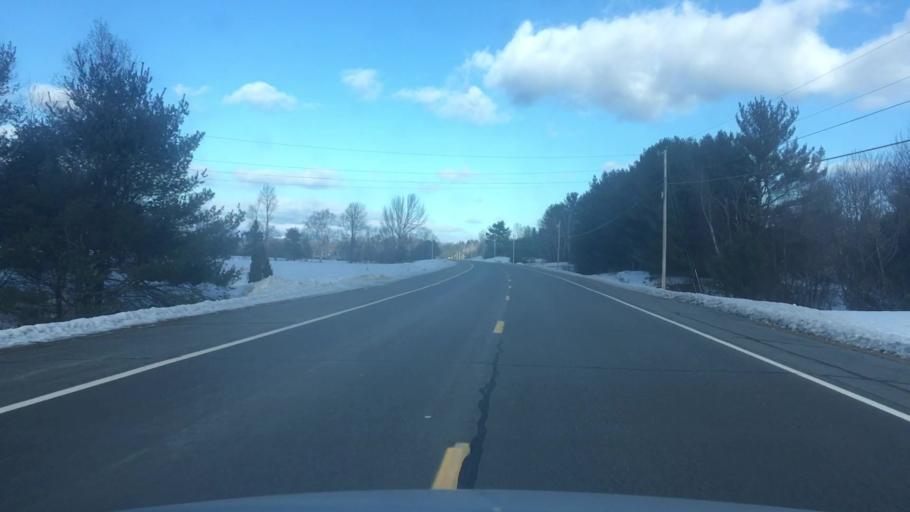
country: US
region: Maine
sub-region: Somerset County
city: Madison
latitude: 45.0152
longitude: -69.8578
